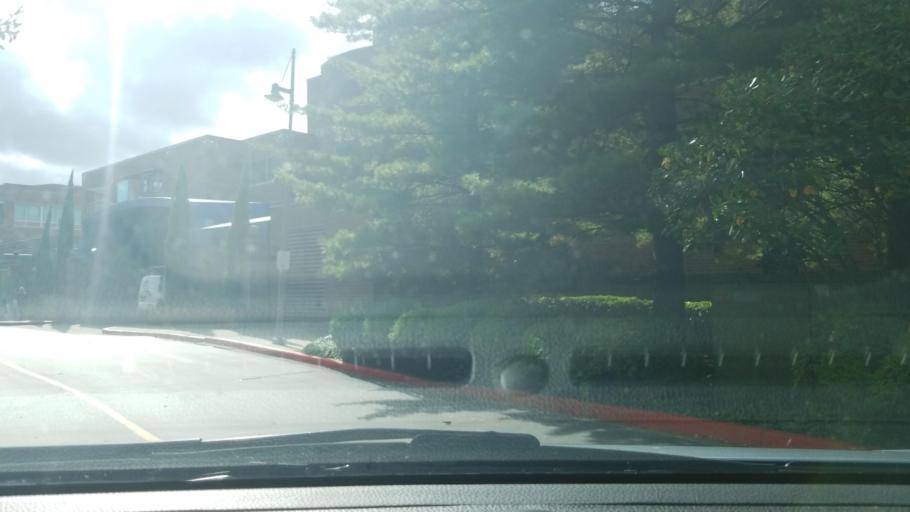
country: US
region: Washington
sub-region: King County
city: Yarrow Point
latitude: 47.6573
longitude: -122.2066
